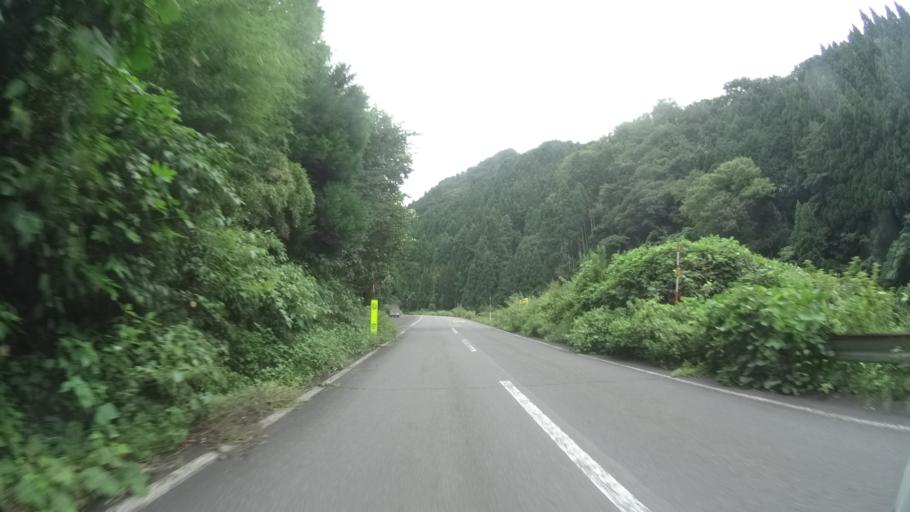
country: JP
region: Tottori
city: Kurayoshi
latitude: 35.4085
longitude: 134.0113
